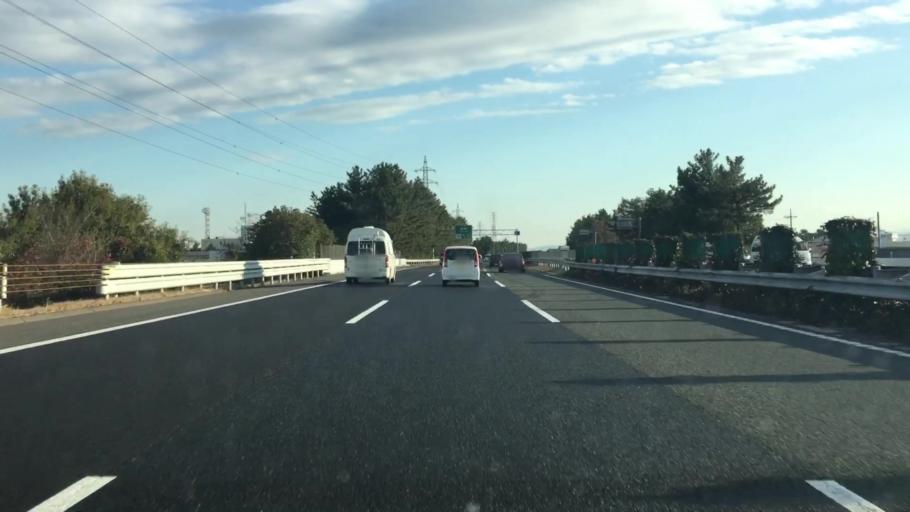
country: JP
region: Gunma
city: Takasaki
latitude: 36.3420
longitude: 139.0562
